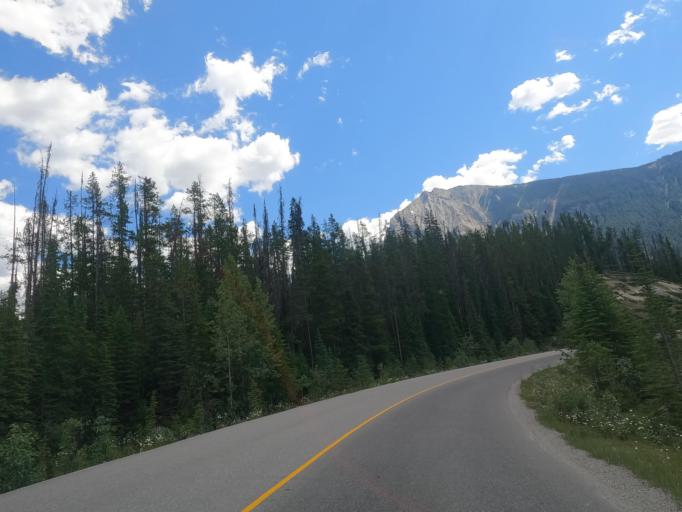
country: CA
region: Alberta
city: Lake Louise
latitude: 51.3832
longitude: -116.5281
